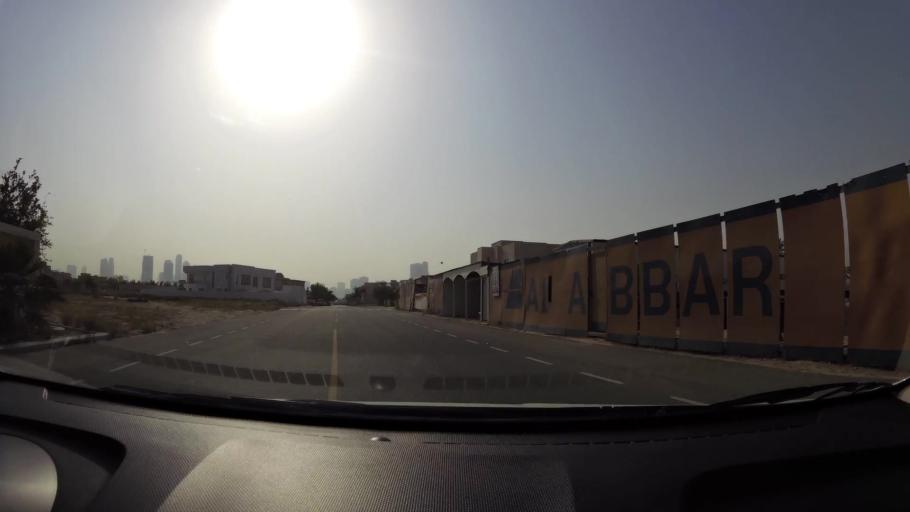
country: AE
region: Ash Shariqah
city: Sharjah
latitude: 25.3077
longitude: 55.3421
